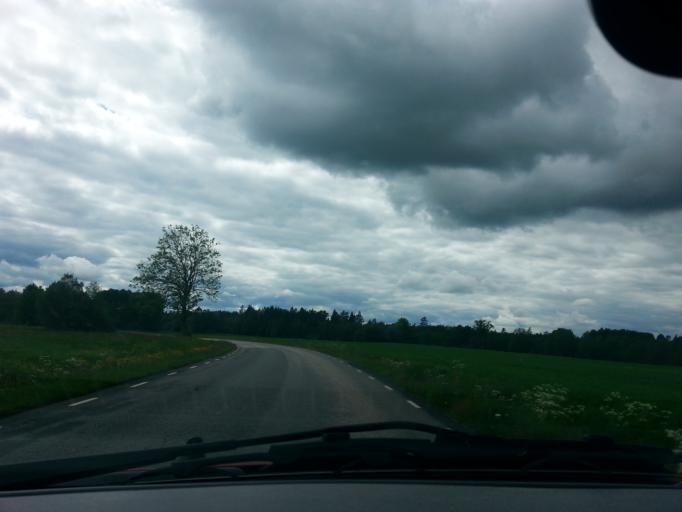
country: SE
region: Joenkoeping
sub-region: Gislaveds Kommun
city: Reftele
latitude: 57.2066
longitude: 13.6018
